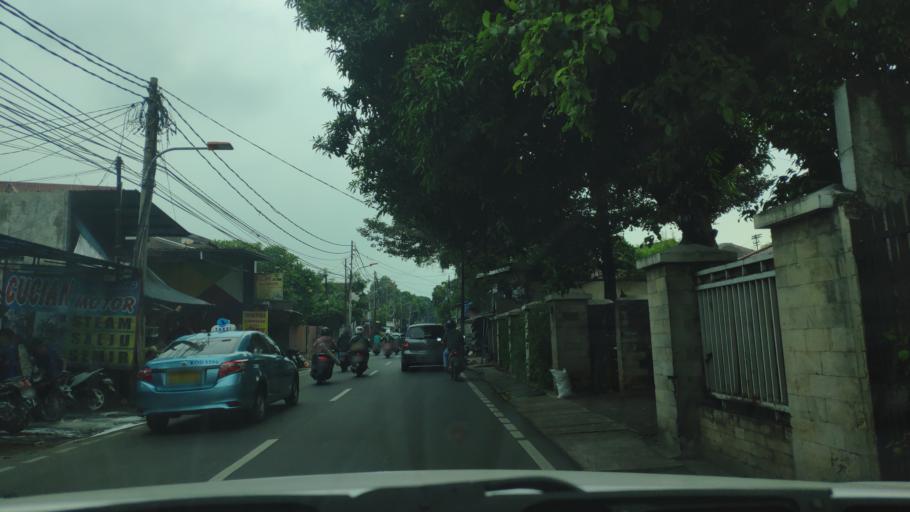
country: ID
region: Jakarta Raya
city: Jakarta
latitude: -6.1903
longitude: 106.7860
